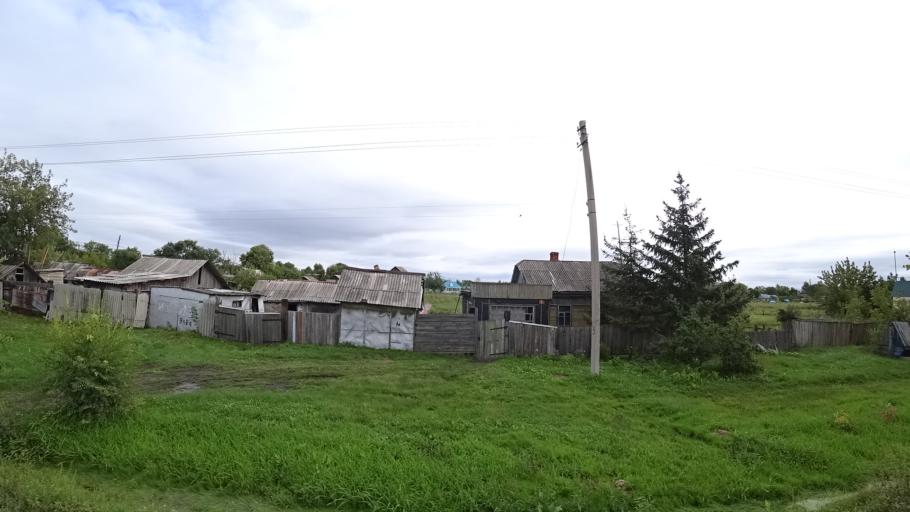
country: RU
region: Primorskiy
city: Chernigovka
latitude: 44.3444
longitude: 132.5608
